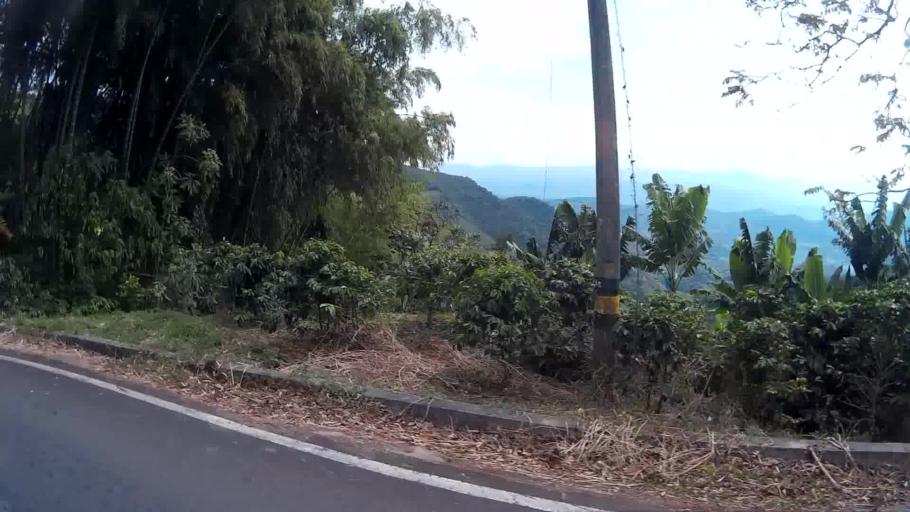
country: CO
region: Risaralda
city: Marsella
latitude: 4.8786
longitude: -75.7606
